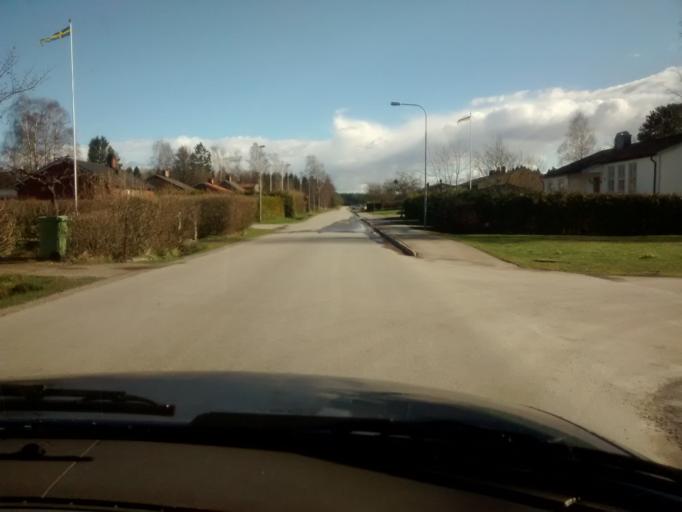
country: SE
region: OEstergoetland
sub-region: Norrkopings Kommun
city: Kimstad
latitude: 58.4659
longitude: 15.8938
